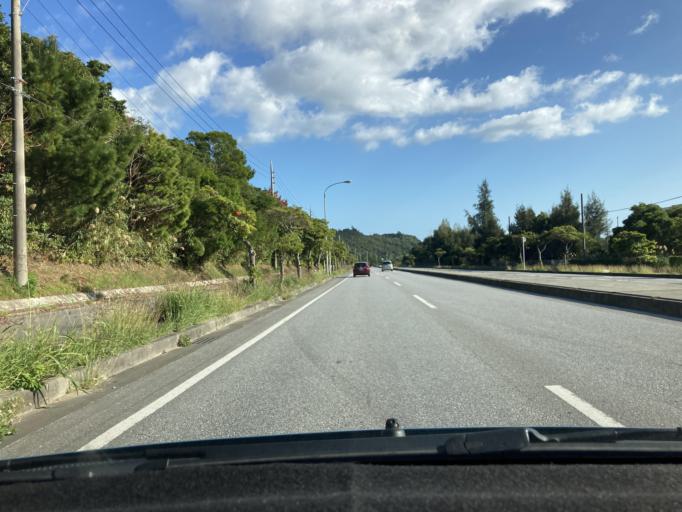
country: JP
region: Okinawa
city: Ishikawa
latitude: 26.4030
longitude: 127.8254
